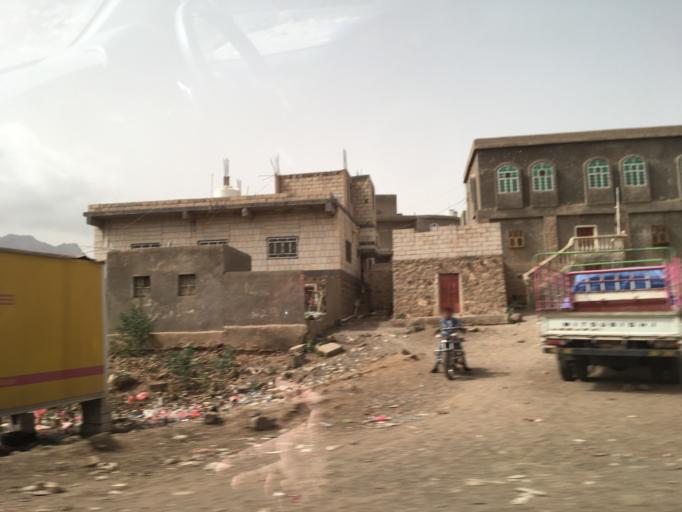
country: YE
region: Ad Dali'
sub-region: Ad Dhale'e
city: Dhalie
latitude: 13.6970
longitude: 44.7310
